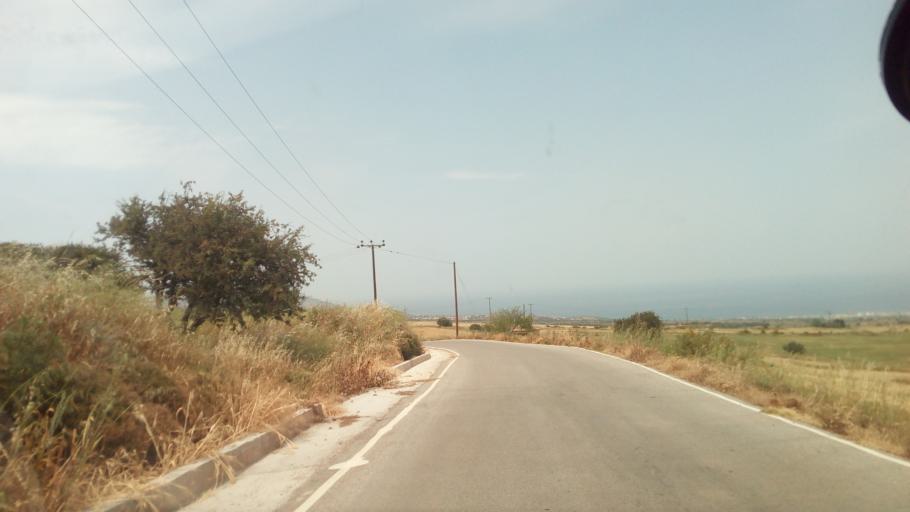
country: CY
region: Pafos
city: Polis
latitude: 34.9885
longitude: 32.3791
